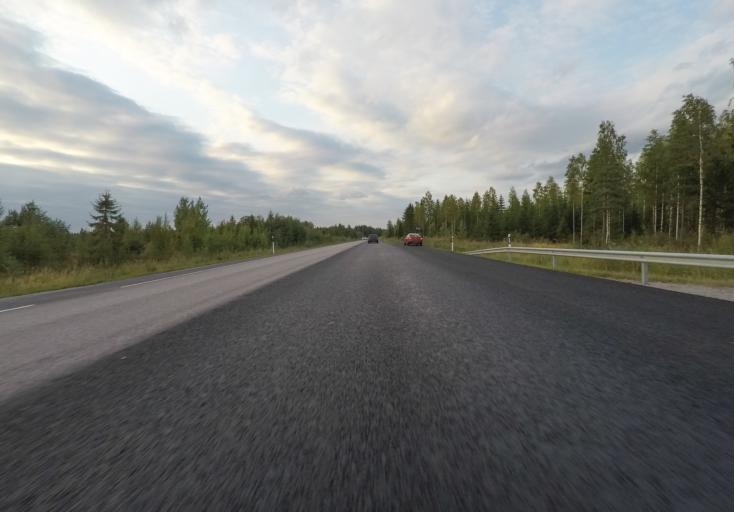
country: FI
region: Paijanne Tavastia
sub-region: Lahti
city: Hartola
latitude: 61.5889
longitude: 26.0093
